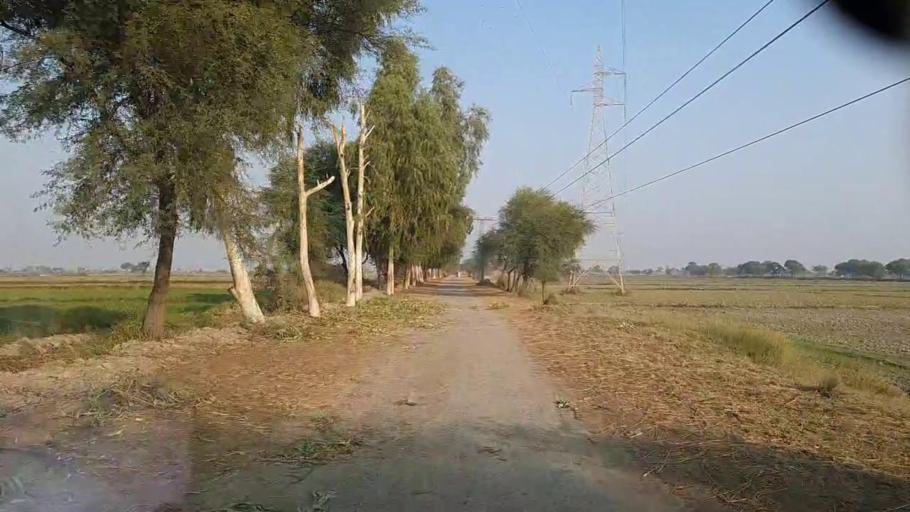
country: PK
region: Sindh
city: Jacobabad
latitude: 28.2402
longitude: 68.4936
